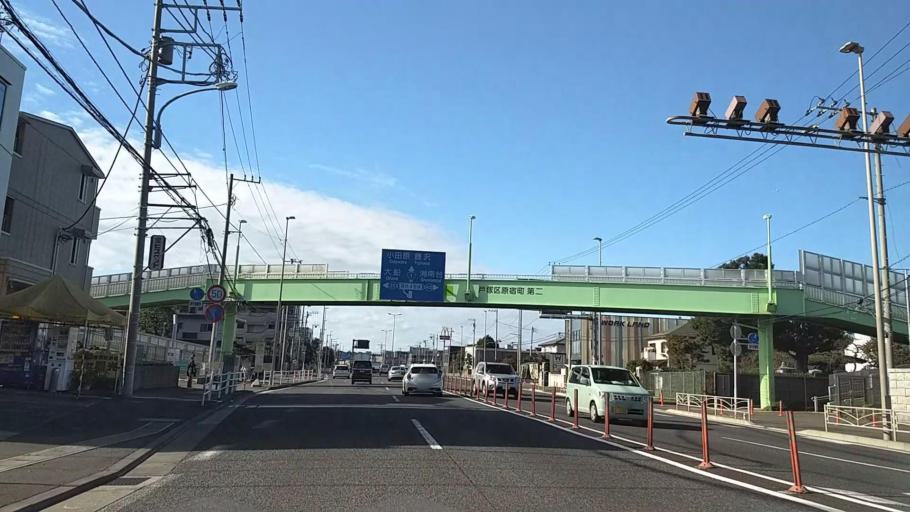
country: JP
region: Kanagawa
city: Fujisawa
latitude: 35.3790
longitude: 139.5091
